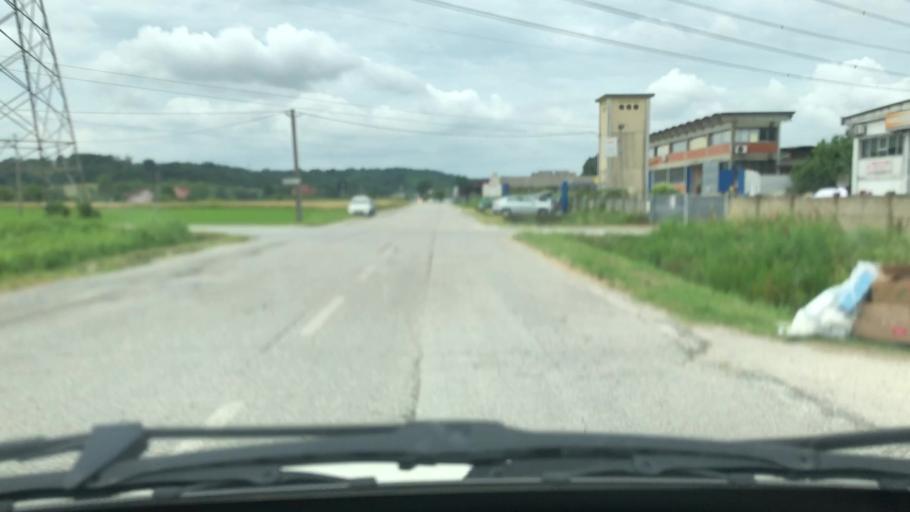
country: IT
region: Tuscany
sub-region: Province of Pisa
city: Bientina
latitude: 43.6991
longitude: 10.6242
